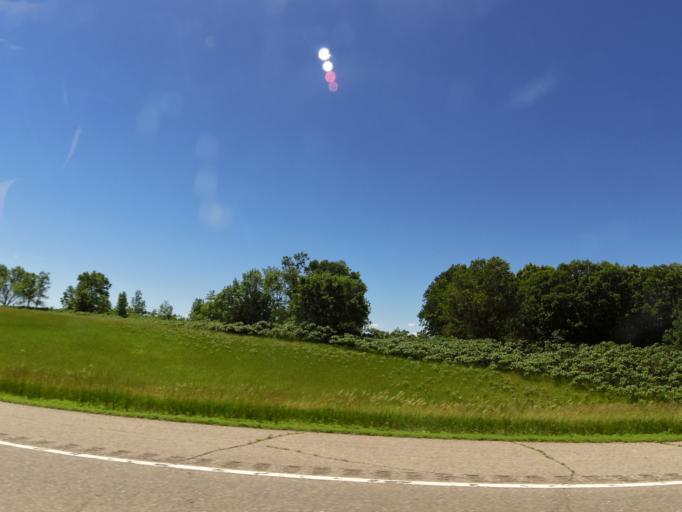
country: US
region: Minnesota
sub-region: Otter Tail County
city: Perham
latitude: 46.6221
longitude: -95.6214
